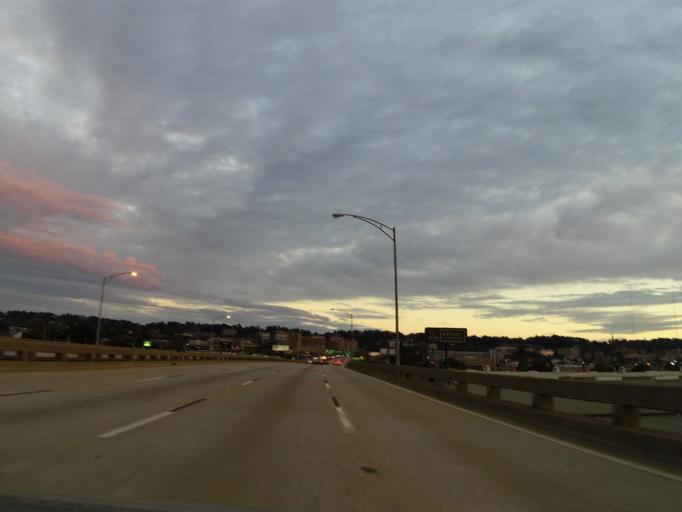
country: US
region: Alabama
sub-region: Jefferson County
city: Birmingham
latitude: 33.5159
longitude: -86.7961
